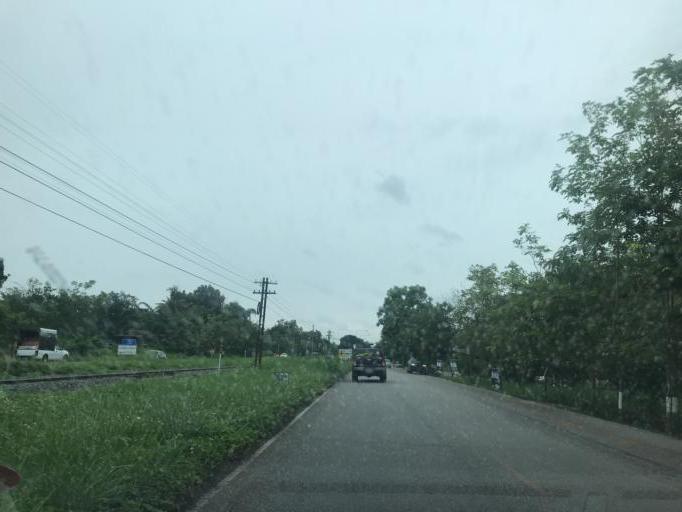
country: TH
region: Chiang Mai
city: Saraphi
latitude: 18.7182
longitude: 99.0383
